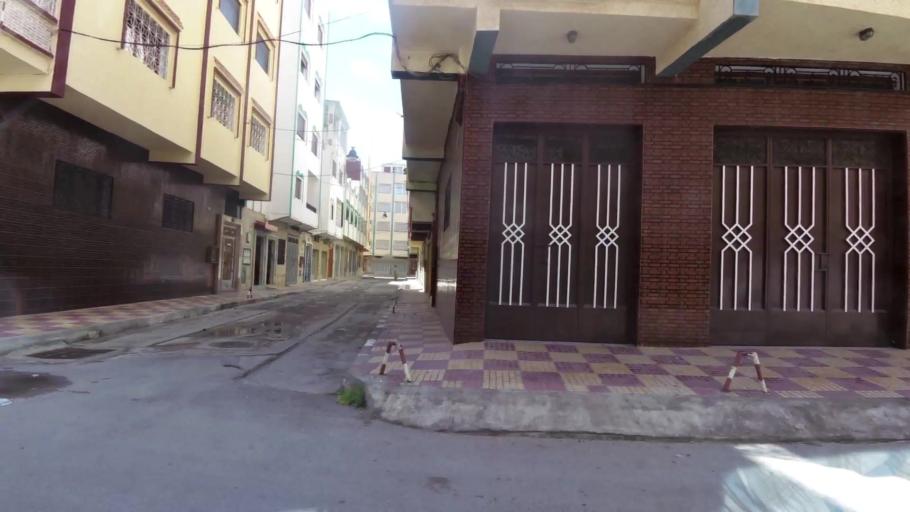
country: MA
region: Tanger-Tetouan
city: Tetouan
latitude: 35.5770
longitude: -5.3458
